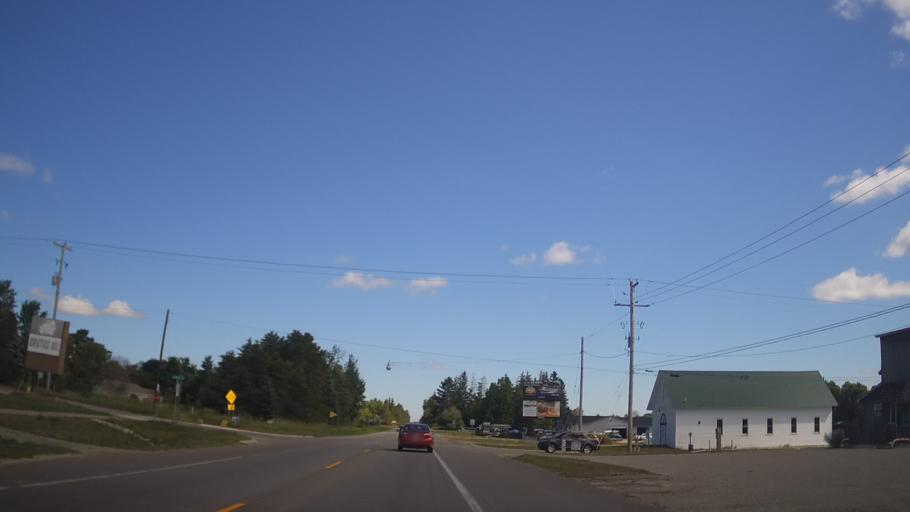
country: US
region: Michigan
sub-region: Cheboygan County
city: Indian River
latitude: 45.4928
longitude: -84.7812
